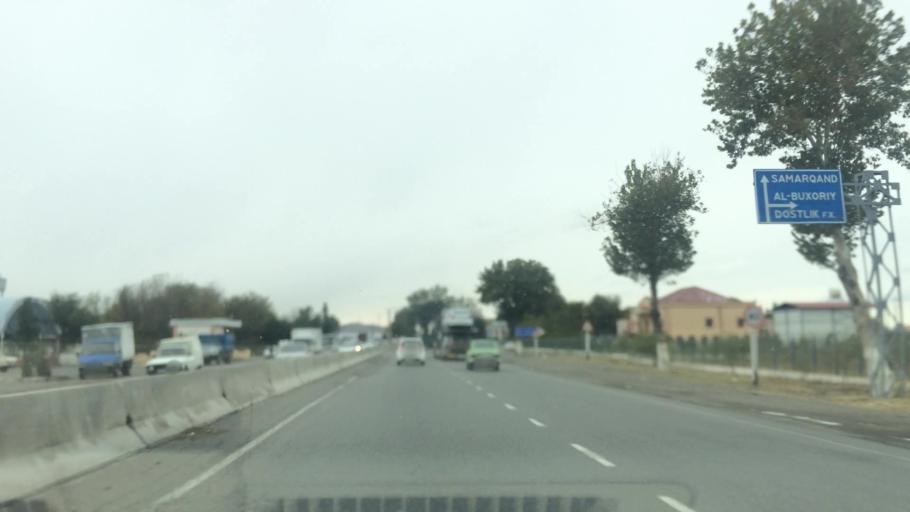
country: UZ
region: Samarqand
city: Jomboy
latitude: 39.7098
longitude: 67.0885
